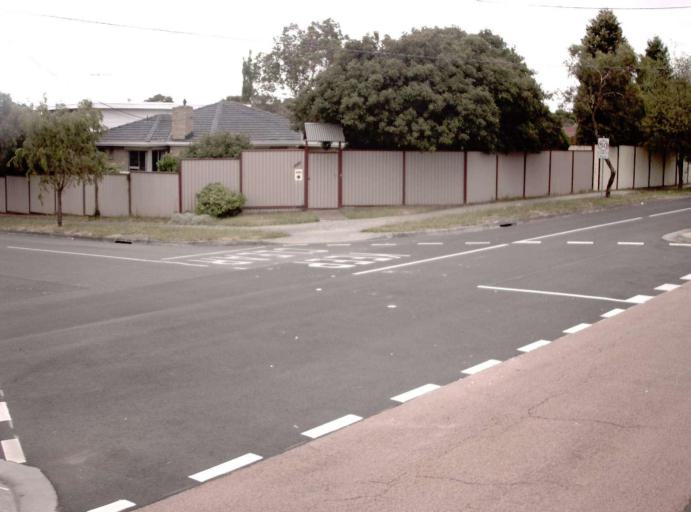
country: AU
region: Victoria
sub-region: Knox
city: Scoresby
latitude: -37.8935
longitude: 145.2329
